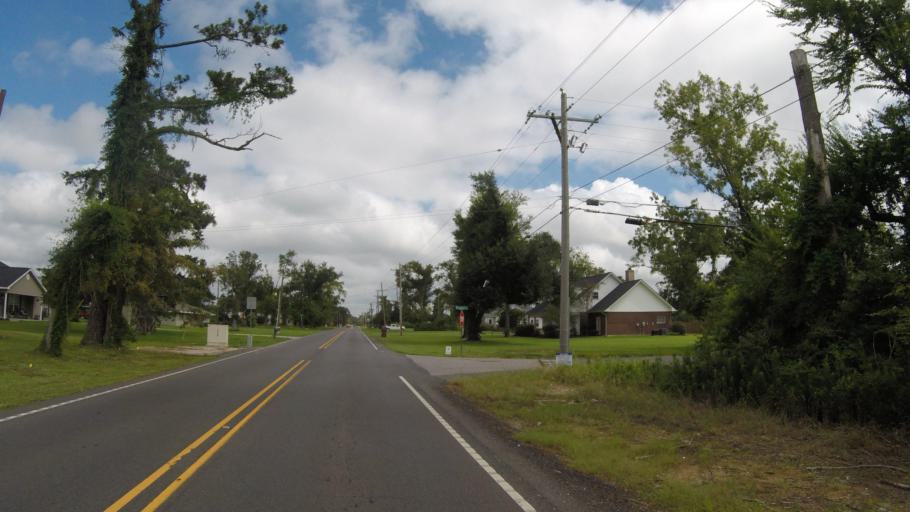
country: US
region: Louisiana
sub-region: Calcasieu Parish
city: Westlake
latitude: 30.2554
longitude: -93.2455
